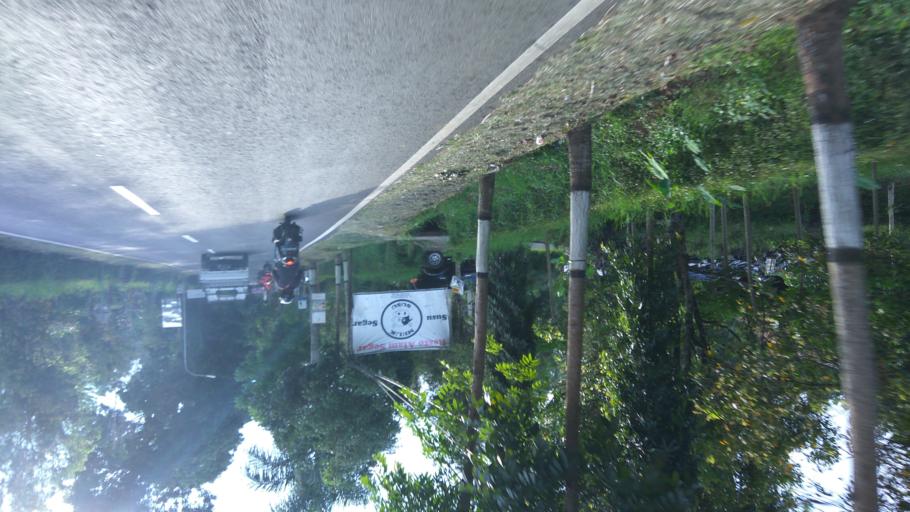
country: ID
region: Central Java
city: Salatiga
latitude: -7.3604
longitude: 110.4780
